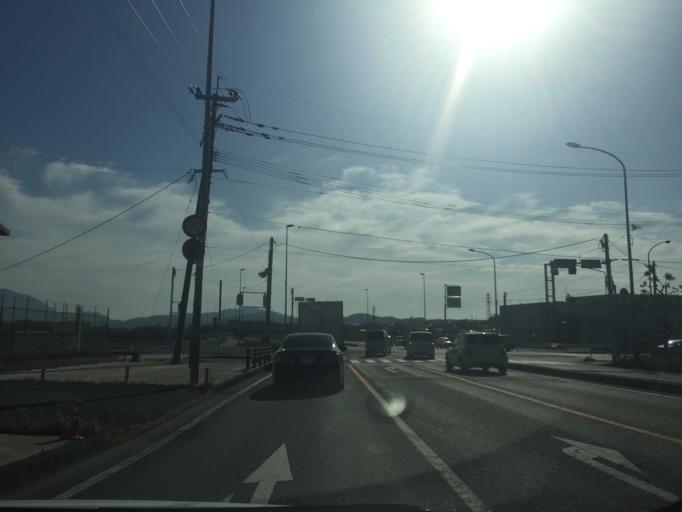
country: JP
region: Fukuoka
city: Fukuoka-shi
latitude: 33.6097
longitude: 130.4624
